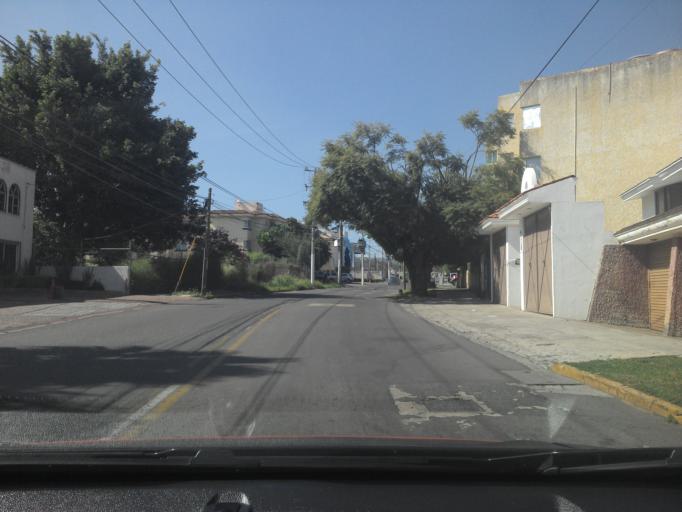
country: MX
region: Jalisco
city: Zapopan2
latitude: 20.6918
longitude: -103.4122
